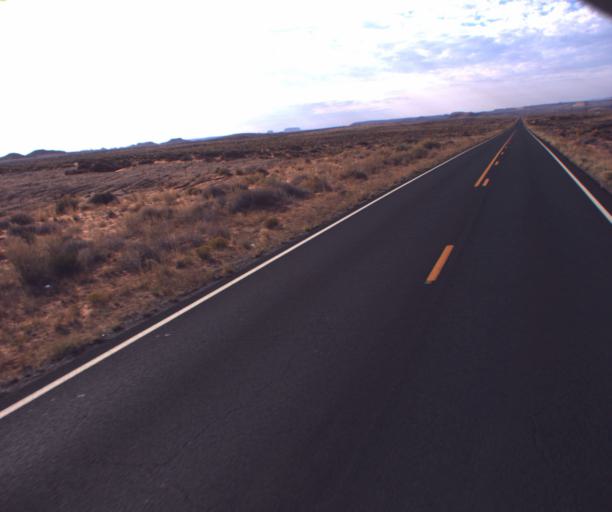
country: US
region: Arizona
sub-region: Apache County
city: Many Farms
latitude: 36.8248
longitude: -109.6447
